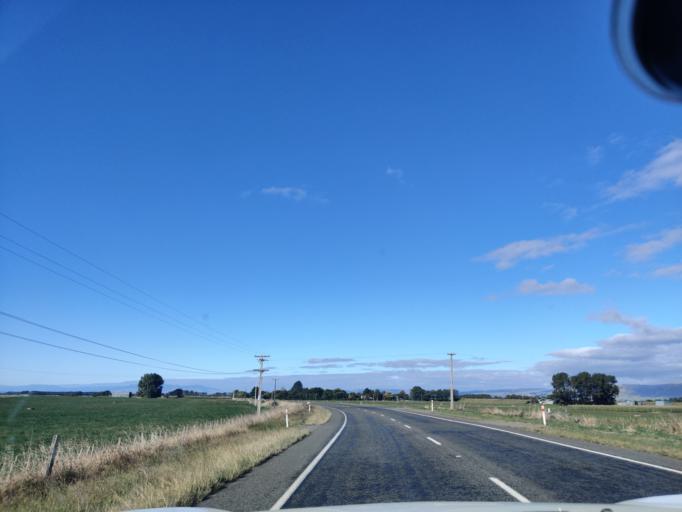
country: NZ
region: Manawatu-Wanganui
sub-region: Horowhenua District
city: Foxton
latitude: -40.4255
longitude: 175.4573
